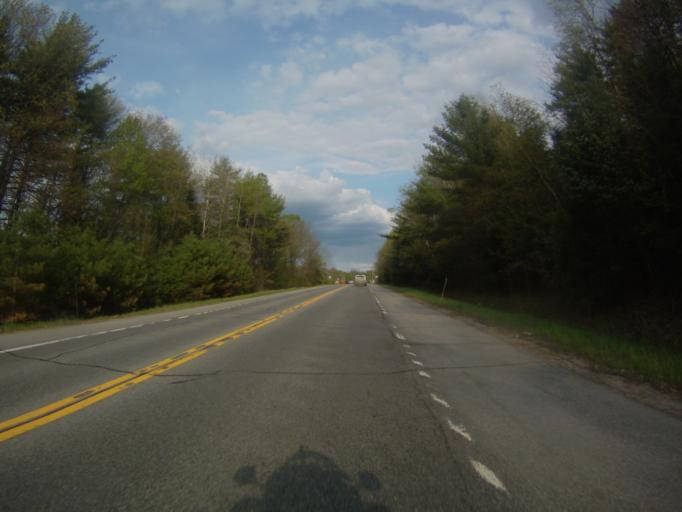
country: US
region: New York
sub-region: Warren County
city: Warrensburg
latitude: 43.6843
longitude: -73.9817
